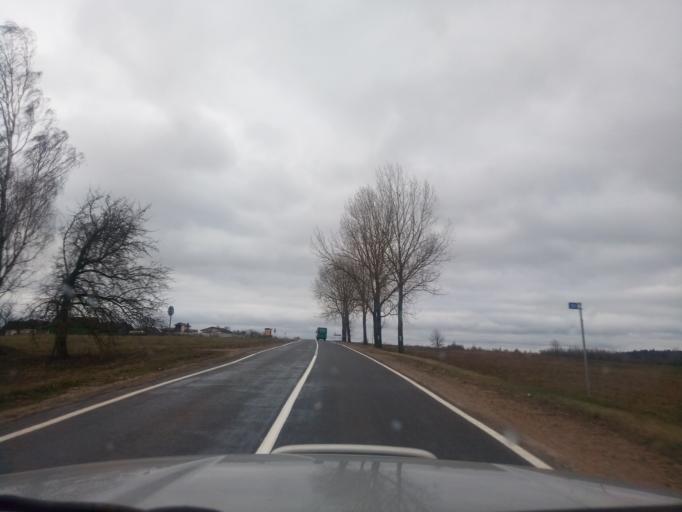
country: BY
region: Minsk
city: Kapyl'
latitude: 53.1776
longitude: 27.1667
